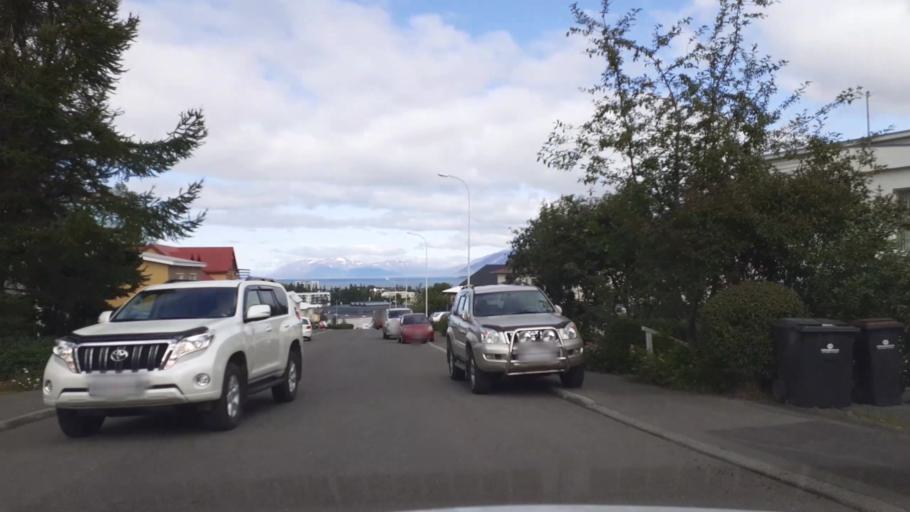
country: IS
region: Northeast
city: Akureyri
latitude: 65.6833
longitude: -18.1036
